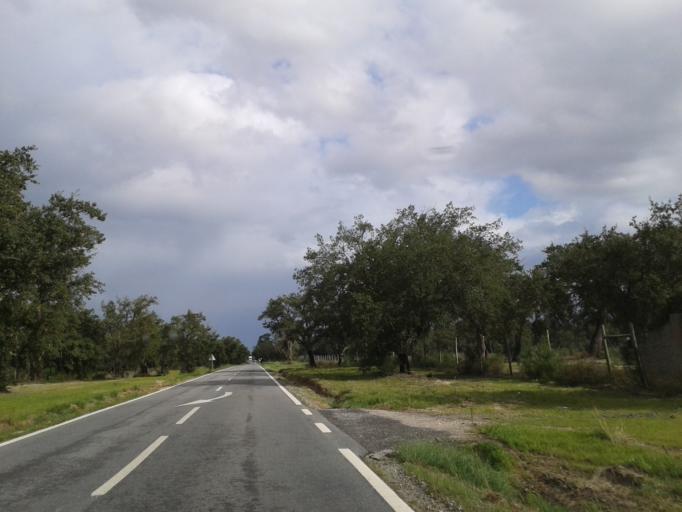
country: PT
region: Santarem
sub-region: Benavente
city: Poceirao
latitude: 38.7897
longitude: -8.8383
